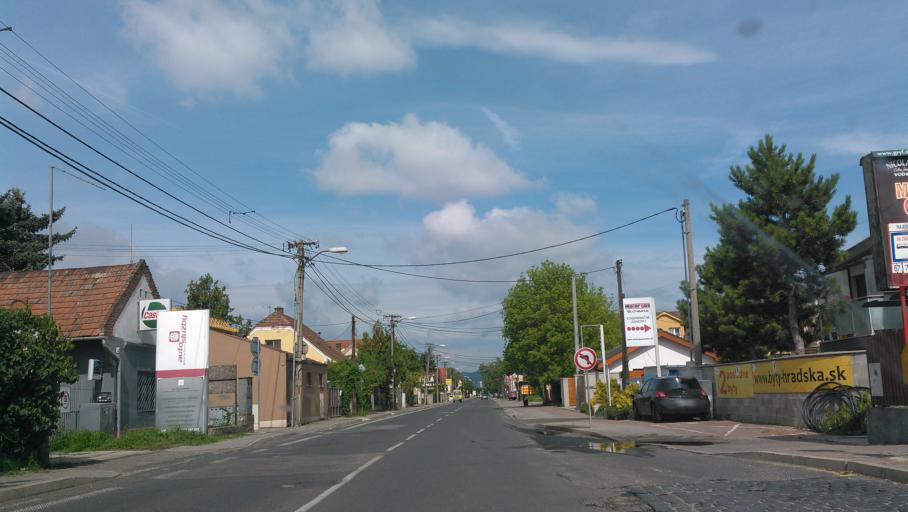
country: SK
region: Bratislavsky
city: Dunajska Luzna
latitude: 48.1518
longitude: 17.2004
